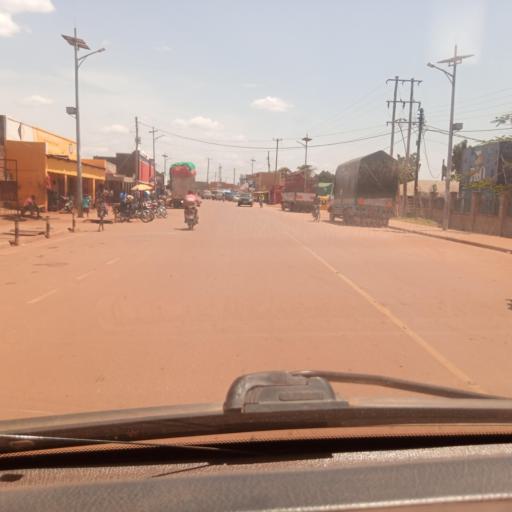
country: UG
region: Northern Region
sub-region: Lira District
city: Lira
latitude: 2.2402
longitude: 32.8918
